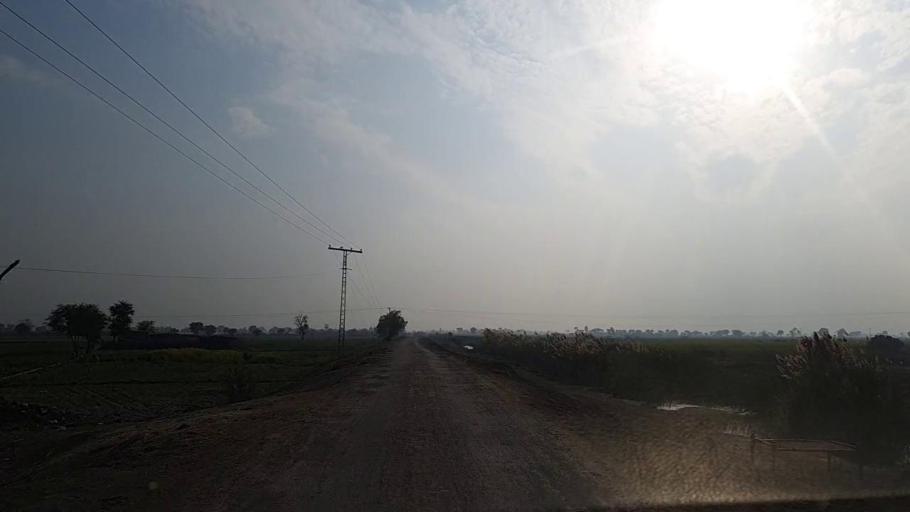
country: PK
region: Sindh
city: Jam Sahib
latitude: 26.3144
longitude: 68.5253
